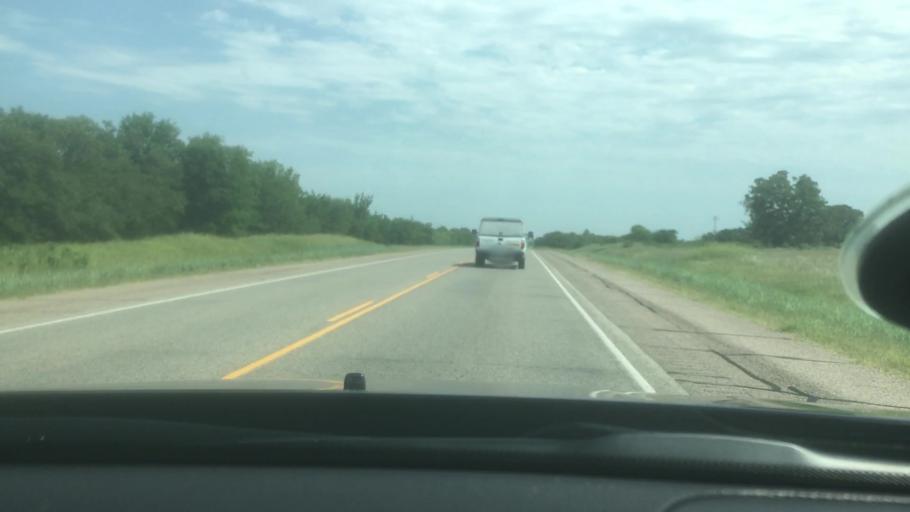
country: US
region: Oklahoma
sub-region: Seminole County
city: Maud
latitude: 35.0410
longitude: -96.9314
